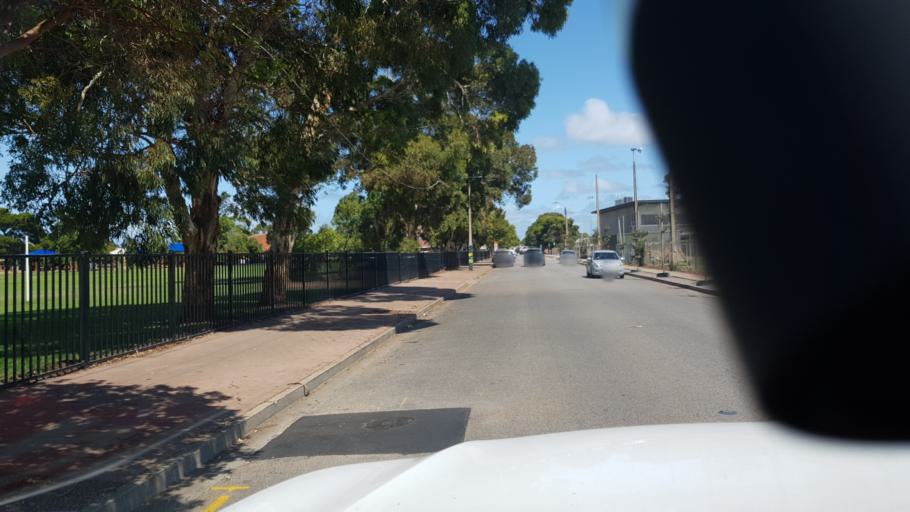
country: AU
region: South Australia
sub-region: Adelaide
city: Brighton
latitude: -35.0152
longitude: 138.5272
